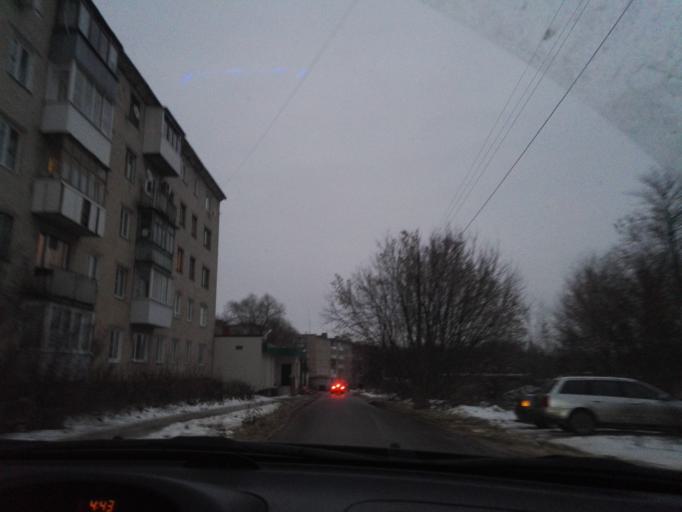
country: RU
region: Tula
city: Novomoskovsk
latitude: 54.0066
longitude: 38.3143
